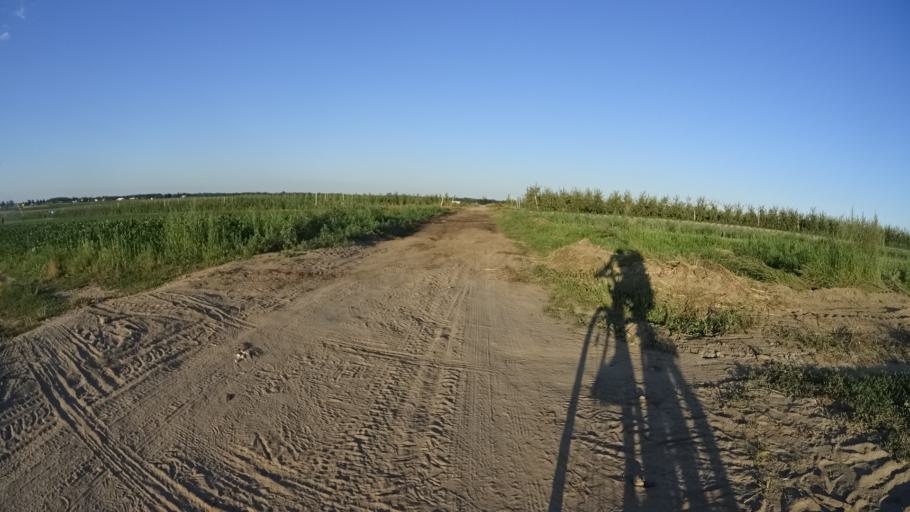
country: PL
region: Masovian Voivodeship
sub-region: Powiat bialobrzeski
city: Wysmierzyce
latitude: 51.6602
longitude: 20.8137
